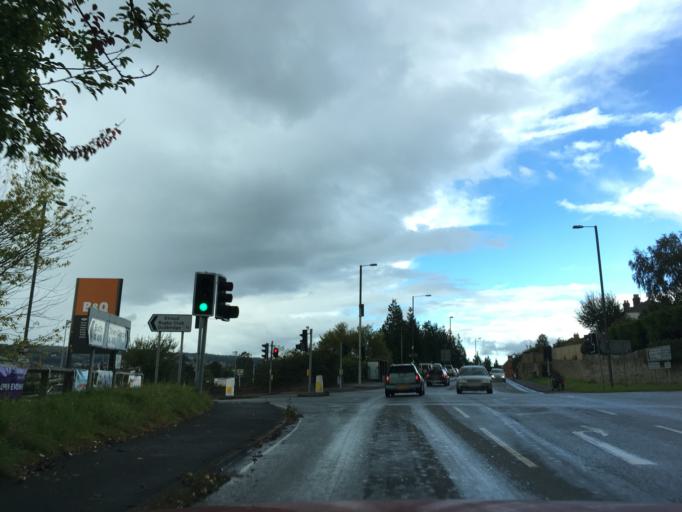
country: GB
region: England
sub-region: Gloucestershire
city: Stroud
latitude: 51.7383
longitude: -2.2318
